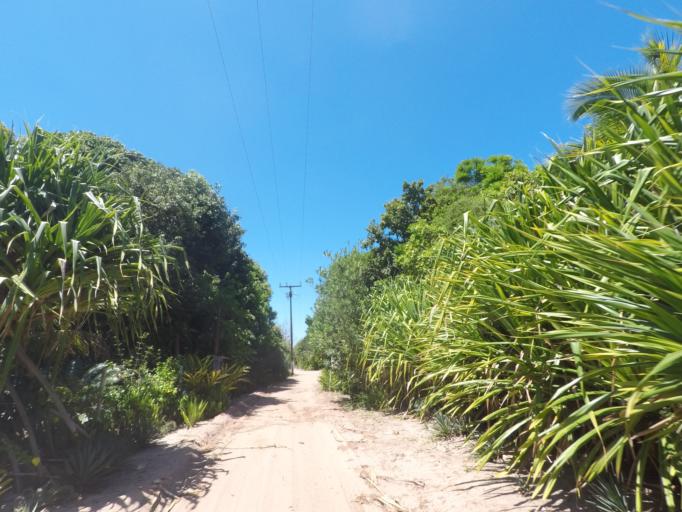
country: BR
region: Bahia
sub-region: Marau
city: Marau
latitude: -14.0105
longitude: -38.9445
